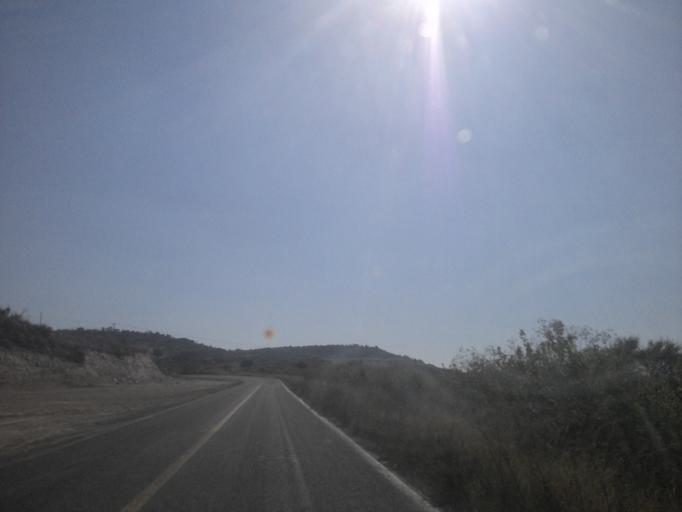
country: MX
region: Jalisco
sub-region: Arandas
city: Santiaguito (Santiaguito de Velazquez)
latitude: 20.7883
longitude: -102.2717
